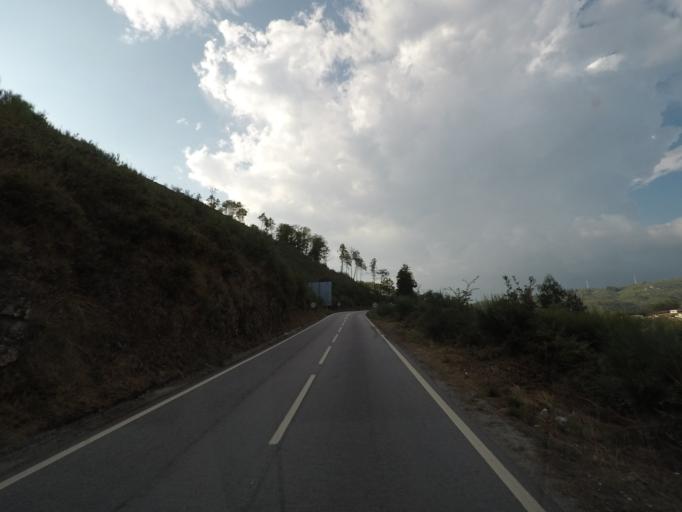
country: PT
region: Porto
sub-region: Baiao
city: Valadares
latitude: 41.1845
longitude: -7.9384
